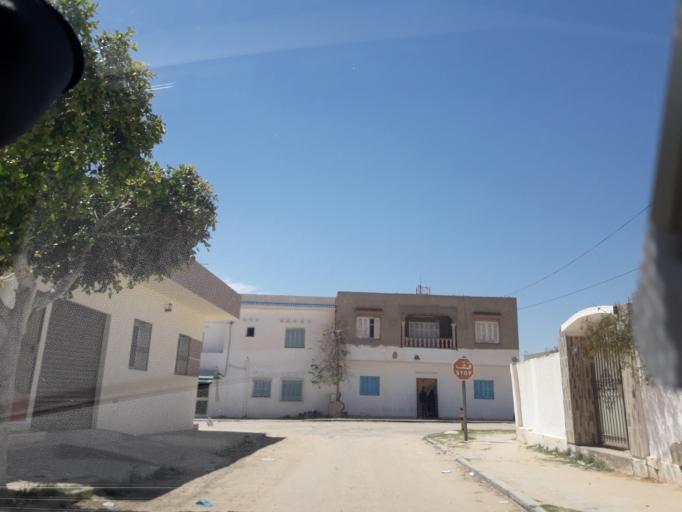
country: TN
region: Safaqis
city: Sfax
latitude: 34.7400
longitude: 10.5218
